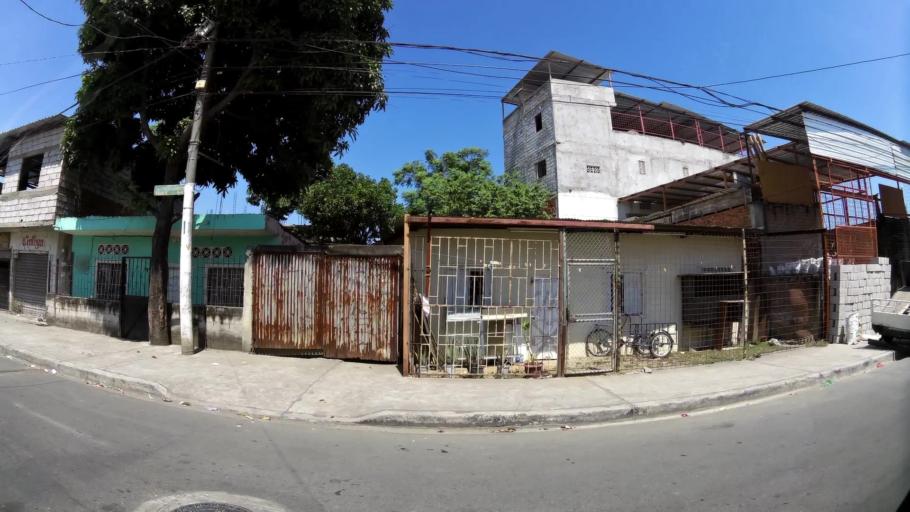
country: EC
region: Guayas
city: Guayaquil
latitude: -2.2367
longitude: -79.9184
